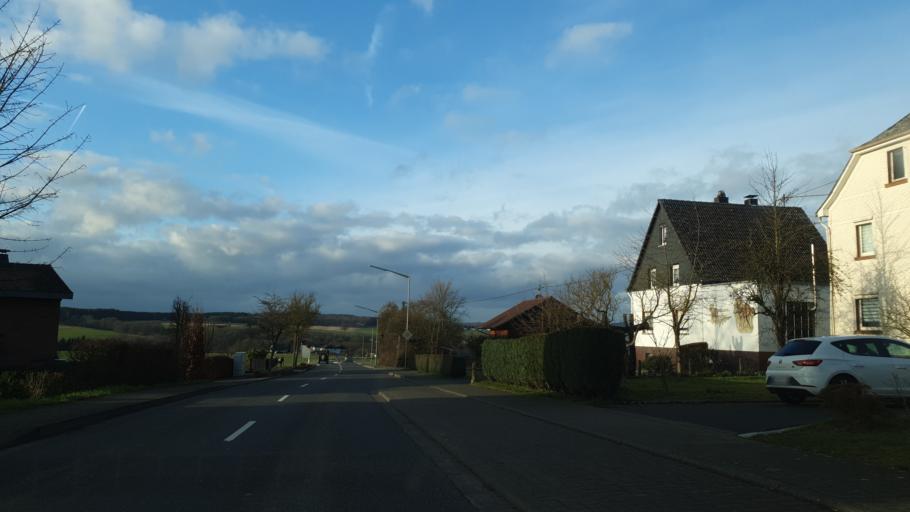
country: DE
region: Rheinland-Pfalz
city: Fluterschen
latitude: 50.6693
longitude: 7.6260
